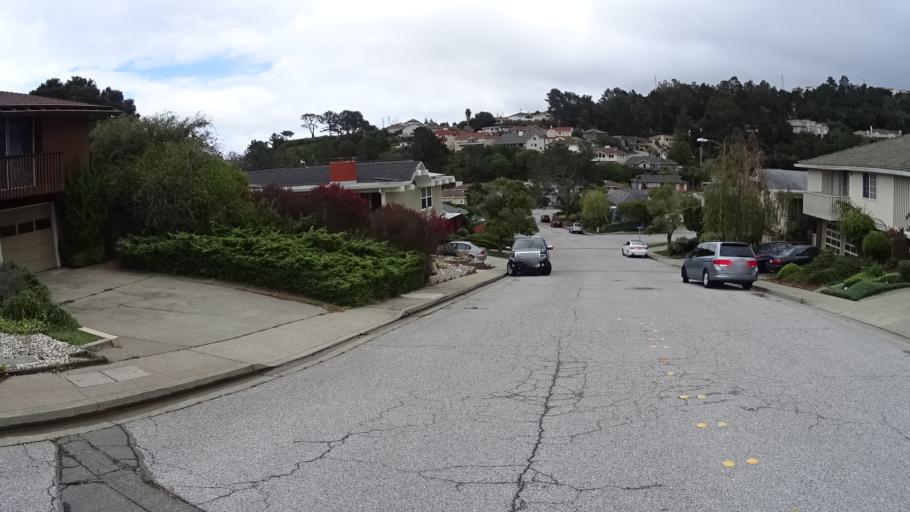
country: US
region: California
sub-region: San Mateo County
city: Millbrae
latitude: 37.6006
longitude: -122.4141
